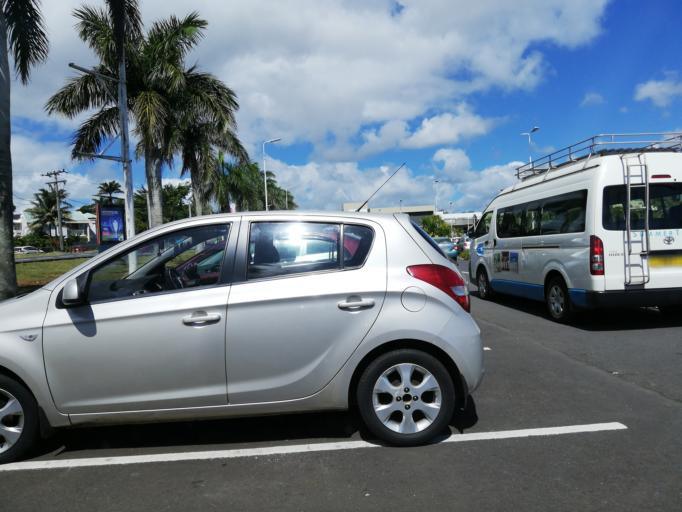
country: MU
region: Plaines Wilhems
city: Quatre Bornes
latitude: -20.2786
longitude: 57.4964
